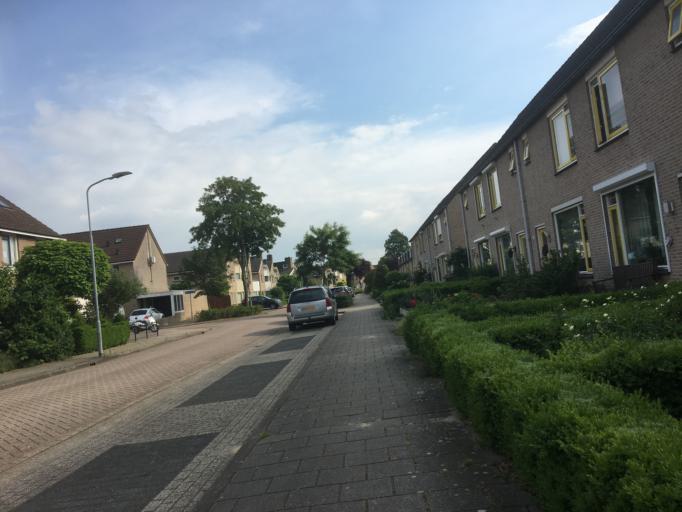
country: NL
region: Gelderland
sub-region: Gemeente Duiven
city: Duiven
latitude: 51.9381
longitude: 6.0098
